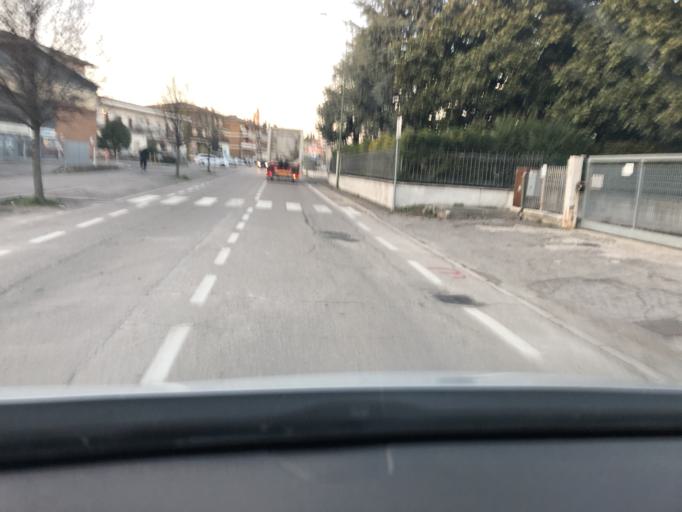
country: IT
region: Veneto
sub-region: Provincia di Verona
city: Sommacampagna
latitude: 45.4010
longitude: 10.8461
